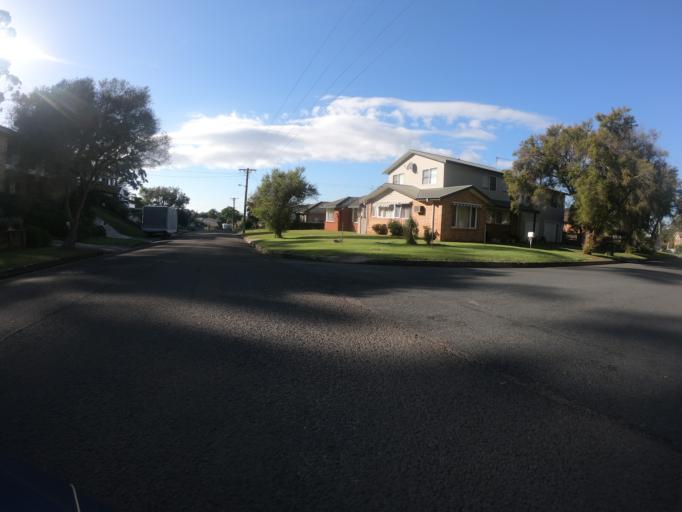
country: AU
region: New South Wales
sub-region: Wollongong
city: Bulli
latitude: -34.3118
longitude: 150.9125
